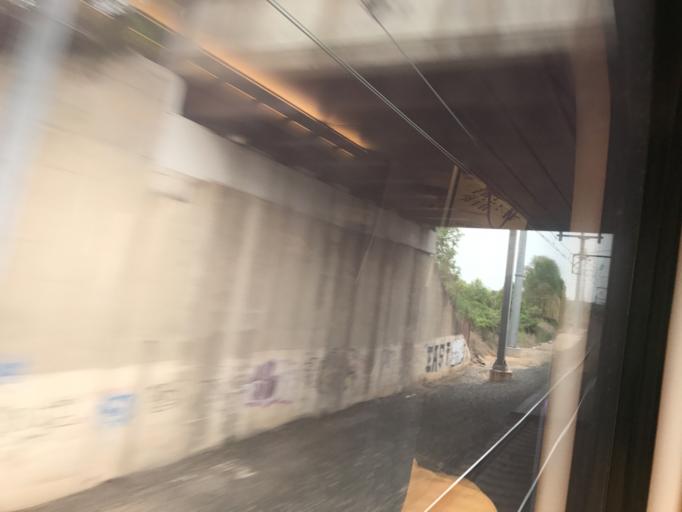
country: US
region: Maryland
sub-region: Prince George's County
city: Cheverly
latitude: 38.9168
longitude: -76.9155
